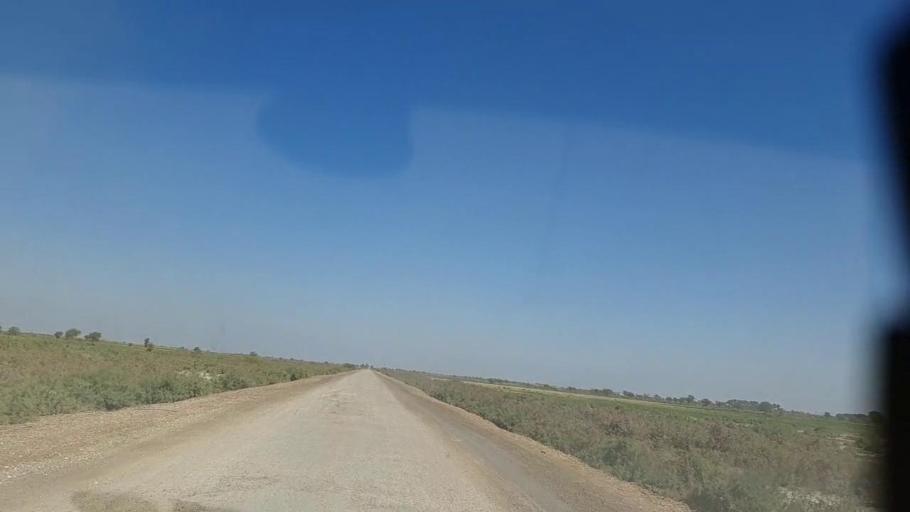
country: PK
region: Sindh
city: Mirwah Gorchani
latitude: 25.2348
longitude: 69.0223
